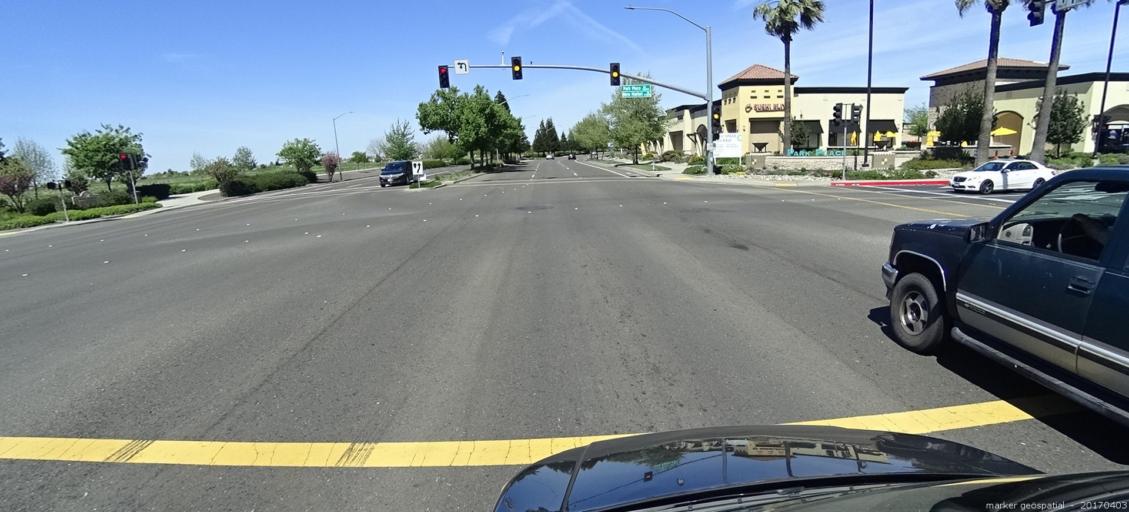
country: US
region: California
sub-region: Sacramento County
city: Rio Linda
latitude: 38.6583
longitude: -121.5120
